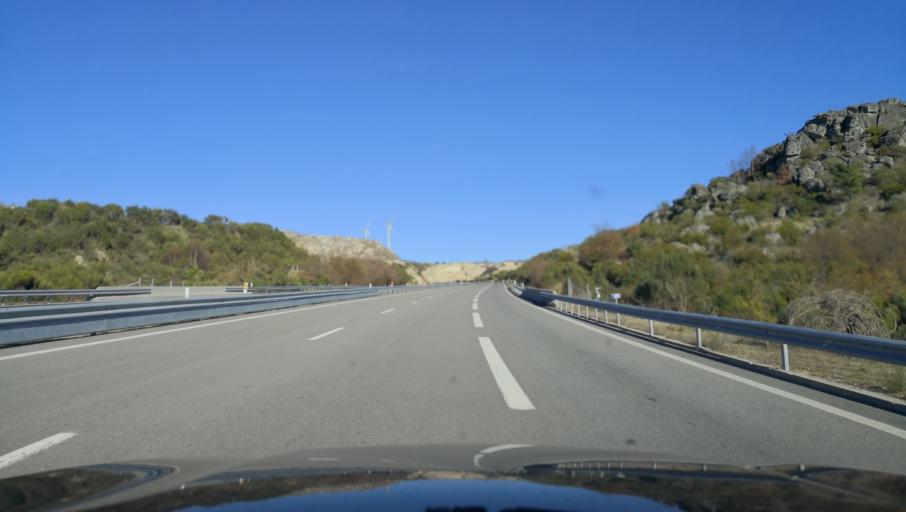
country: PT
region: Vila Real
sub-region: Vila Pouca de Aguiar
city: Vila Pouca de Aguiar
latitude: 41.4010
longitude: -7.6473
